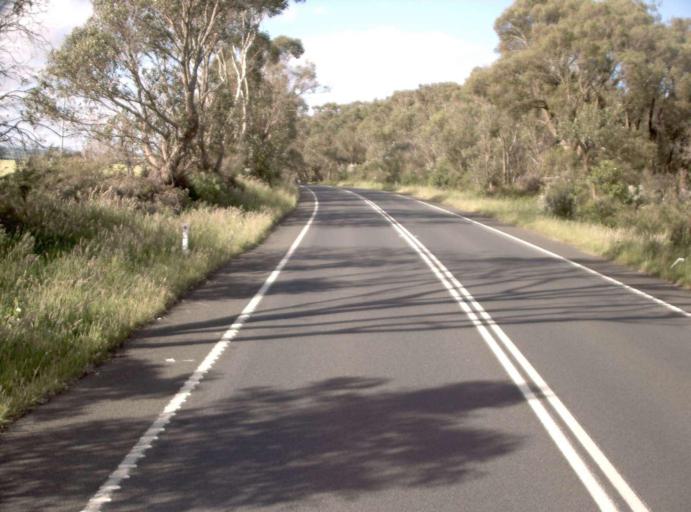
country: AU
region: Victoria
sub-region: Bass Coast
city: North Wonthaggi
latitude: -38.5615
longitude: 145.8418
